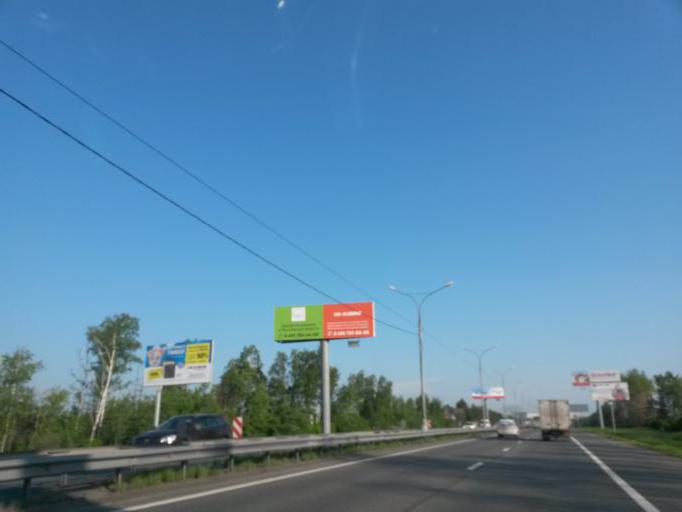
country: RU
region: Moskovskaya
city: Petrovskaya
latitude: 55.5222
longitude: 37.8217
